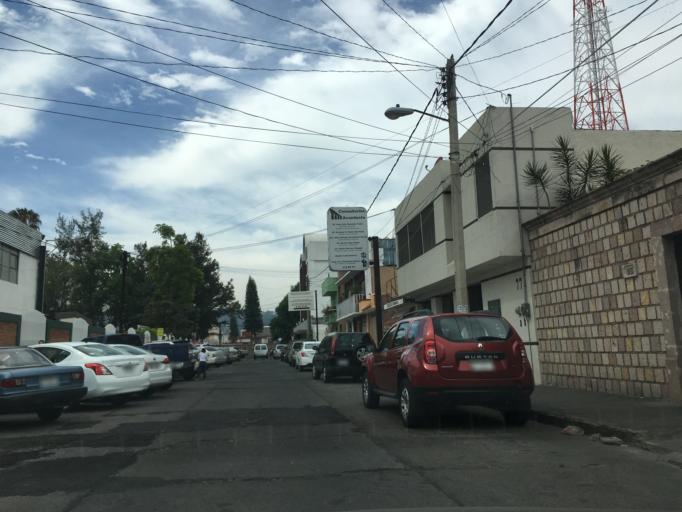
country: MX
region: Michoacan
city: Morelia
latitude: 19.6985
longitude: -101.1713
